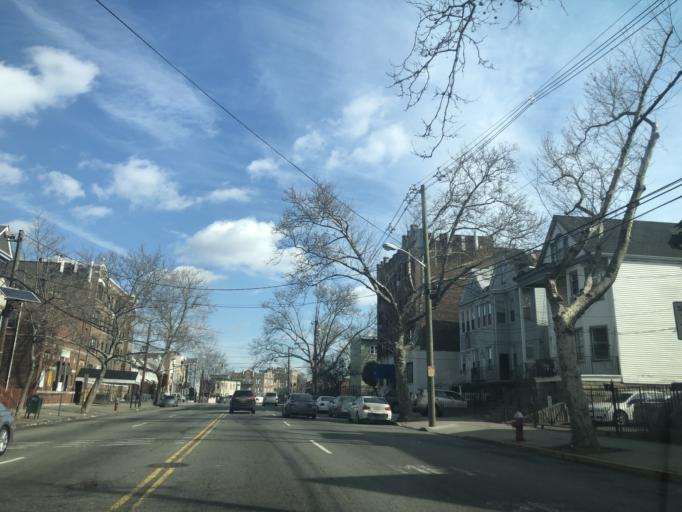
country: US
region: New Jersey
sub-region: Hudson County
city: Jersey City
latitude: 40.7160
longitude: -74.0816
